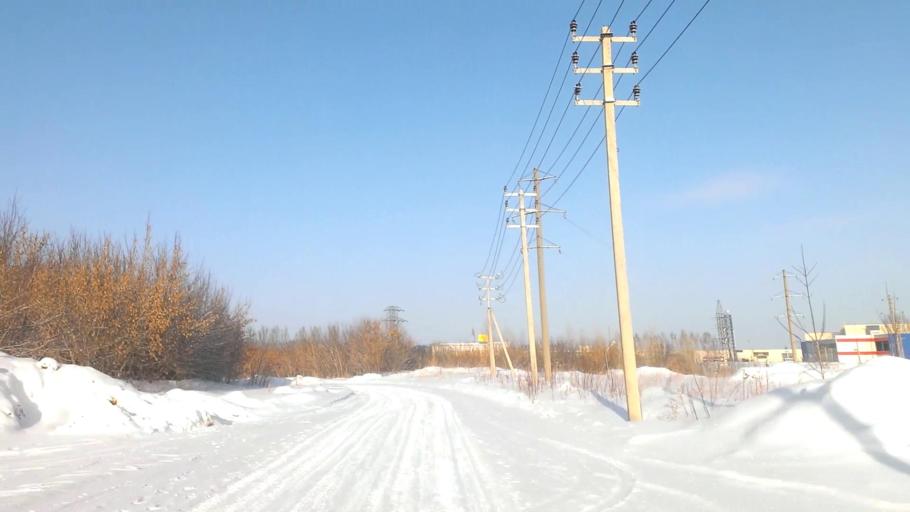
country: RU
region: Altai Krai
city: Novosilikatnyy
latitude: 53.3444
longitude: 83.6300
